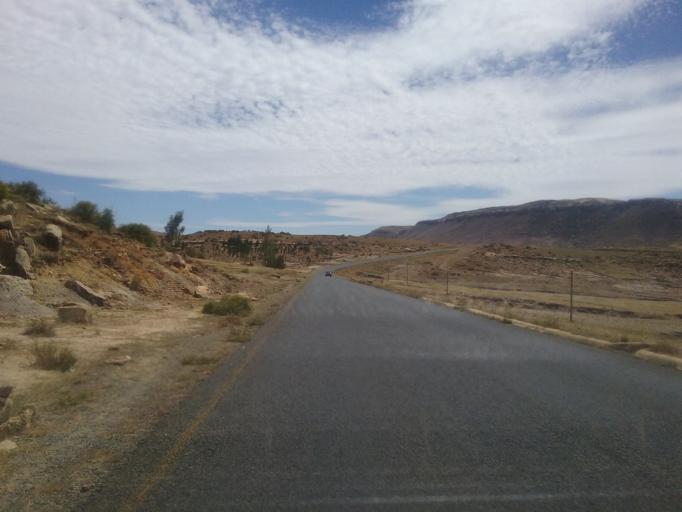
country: LS
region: Mafeteng
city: Mafeteng
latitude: -29.9046
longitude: 27.2515
